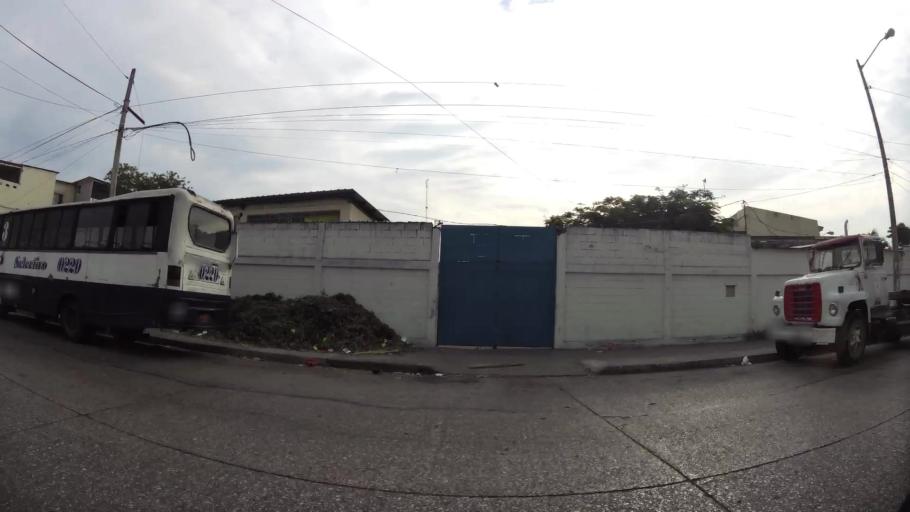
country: EC
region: Guayas
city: Guayaquil
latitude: -2.2472
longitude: -79.9029
